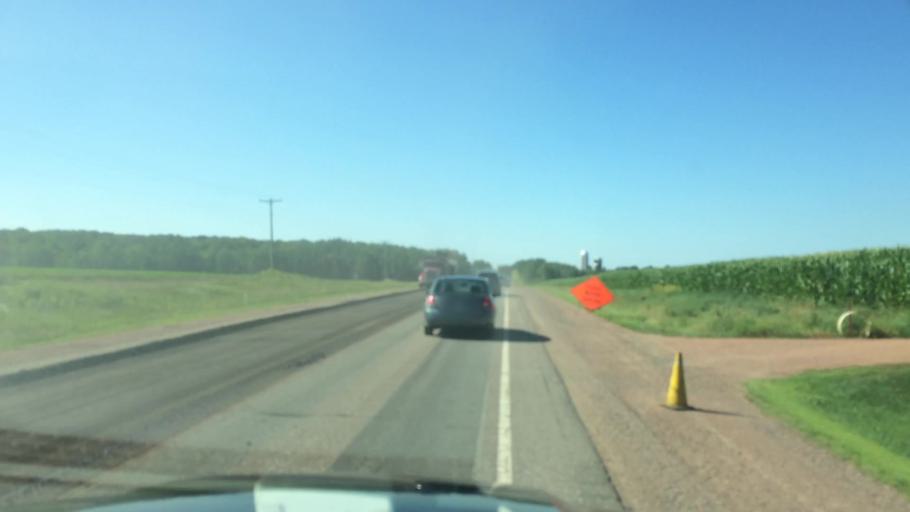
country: US
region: Wisconsin
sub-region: Marathon County
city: Stratford
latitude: 44.9001
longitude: -90.0787
